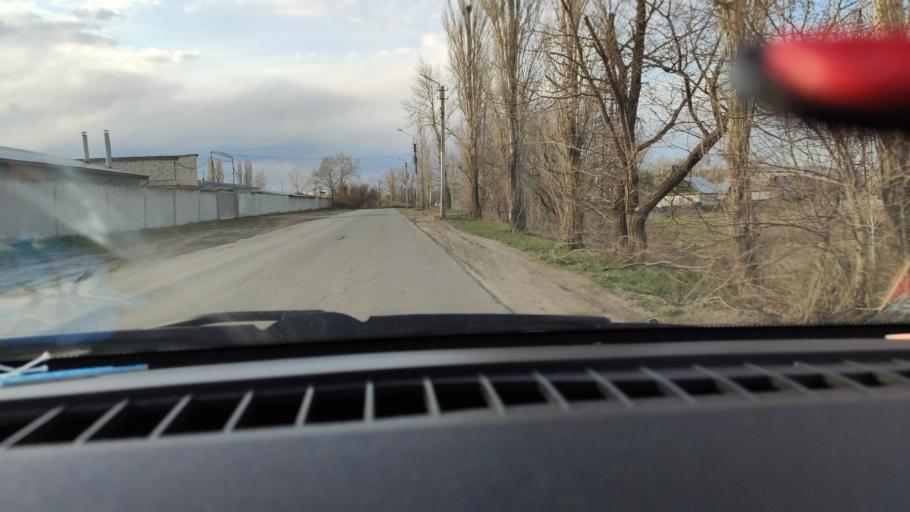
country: RU
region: Saratov
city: Engel's
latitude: 51.4913
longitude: 46.0518
